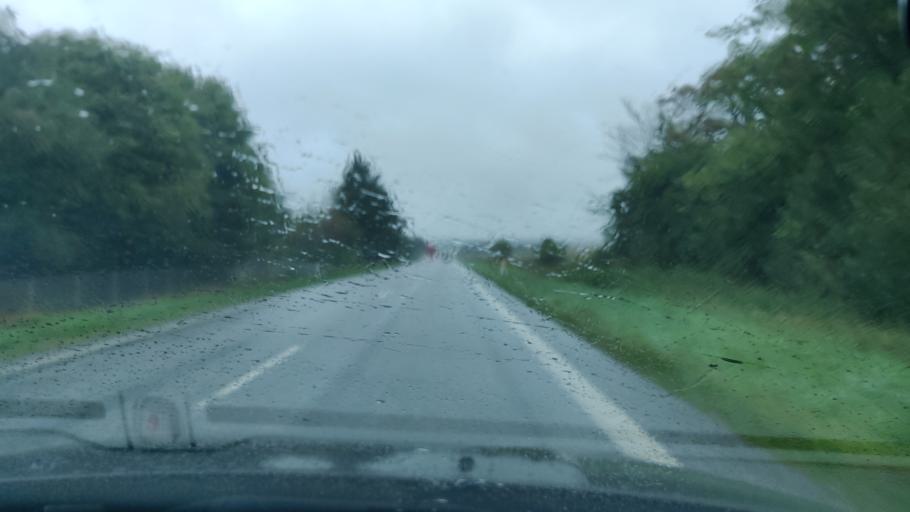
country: DK
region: North Denmark
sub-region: Thisted Kommune
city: Hurup
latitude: 56.8181
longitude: 8.4907
